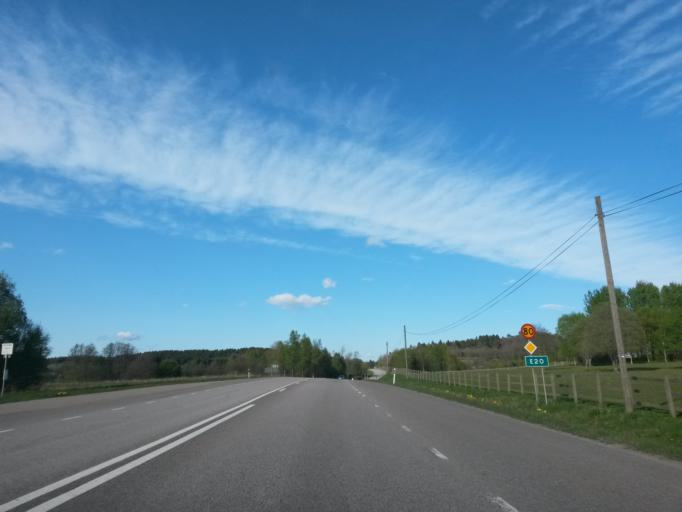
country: SE
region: Vaestra Goetaland
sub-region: Alingsas Kommun
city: Alingsas
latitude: 57.9361
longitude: 12.5795
